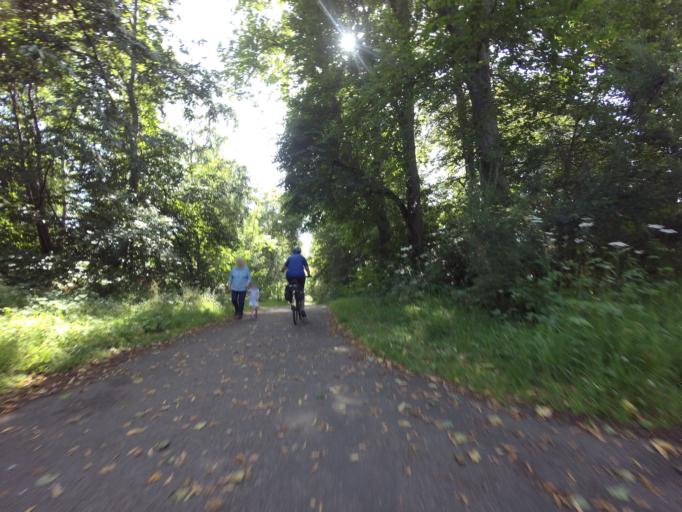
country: GB
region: Scotland
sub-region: Highland
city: Inverness
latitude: 57.4859
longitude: -4.1413
